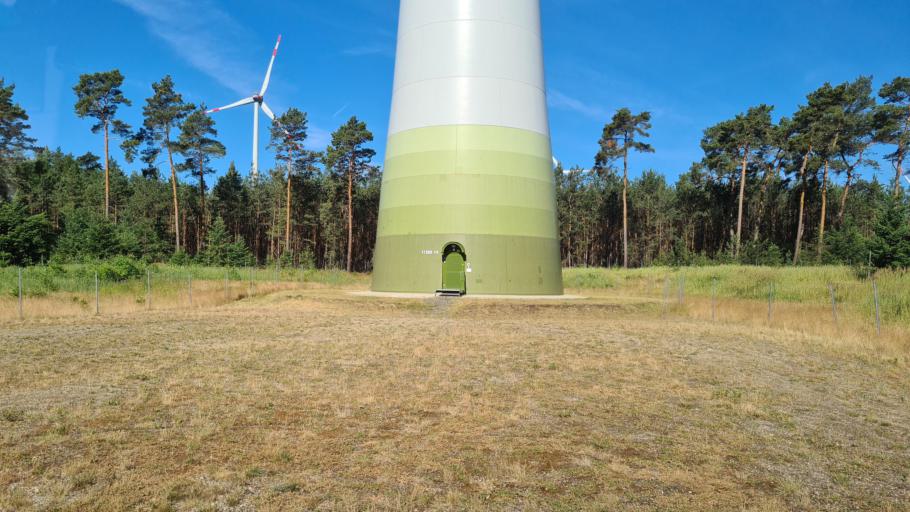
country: DE
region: Brandenburg
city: Treuenbrietzen
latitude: 52.0168
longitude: 12.8591
